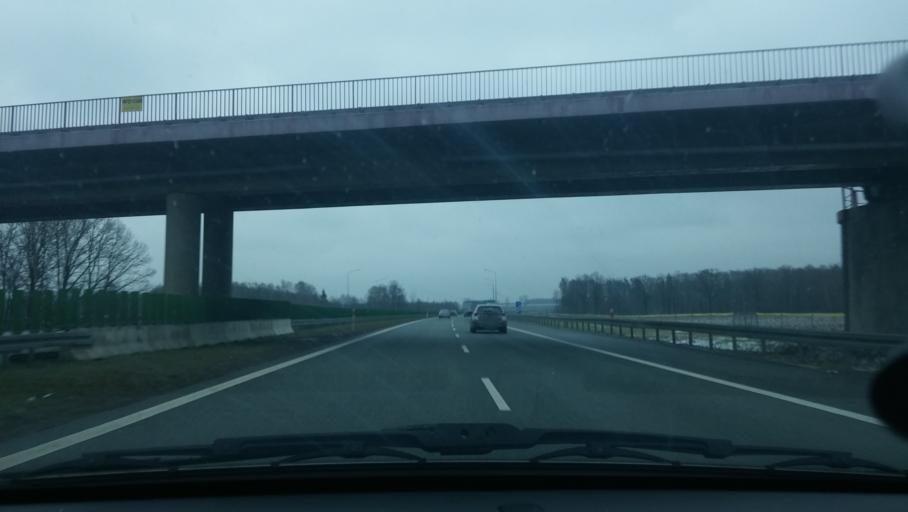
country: PL
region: Masovian Voivodeship
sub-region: Powiat minski
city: Jakubow
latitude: 52.2164
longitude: 21.6338
